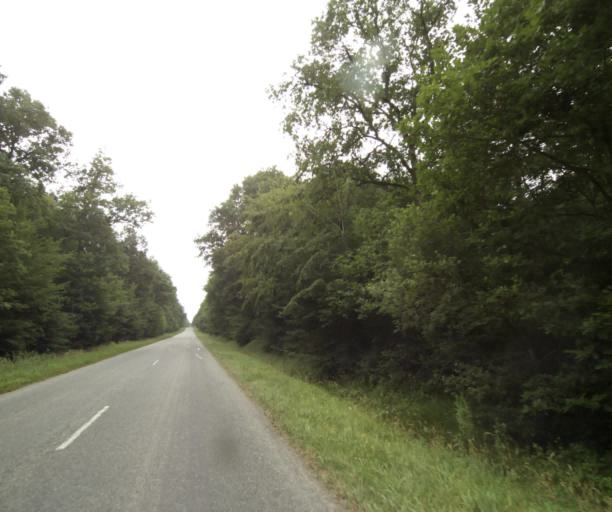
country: FR
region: Centre
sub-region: Departement du Loiret
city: Chanteau
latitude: 47.9621
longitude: 1.9563
